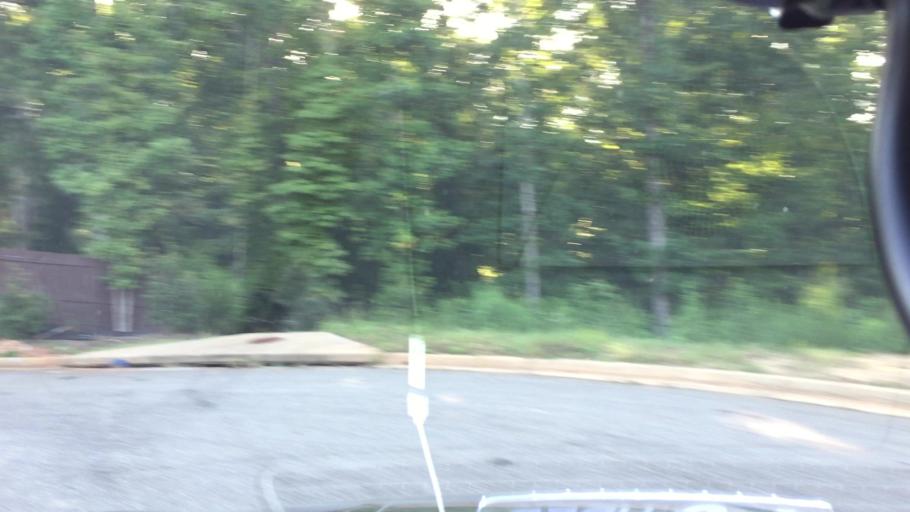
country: US
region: Alabama
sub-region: Lee County
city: Auburn
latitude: 32.5708
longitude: -85.4443
